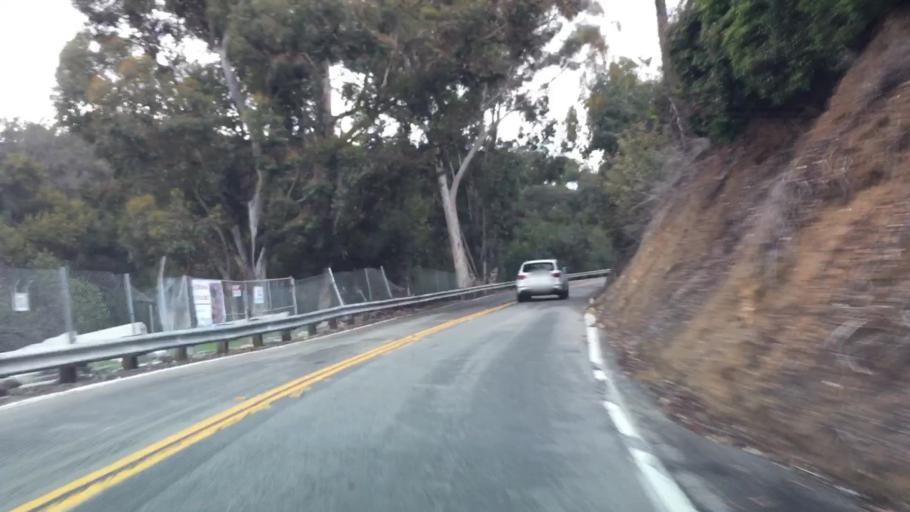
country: US
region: California
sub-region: Los Angeles County
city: Hacienda Heights
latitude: 33.9953
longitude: -117.9902
